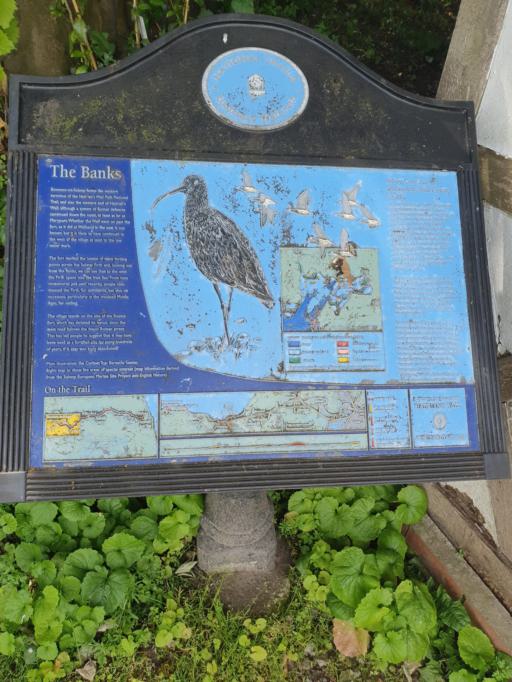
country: GB
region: Scotland
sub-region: Dumfries and Galloway
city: Annan
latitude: 54.9539
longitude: -3.2128
